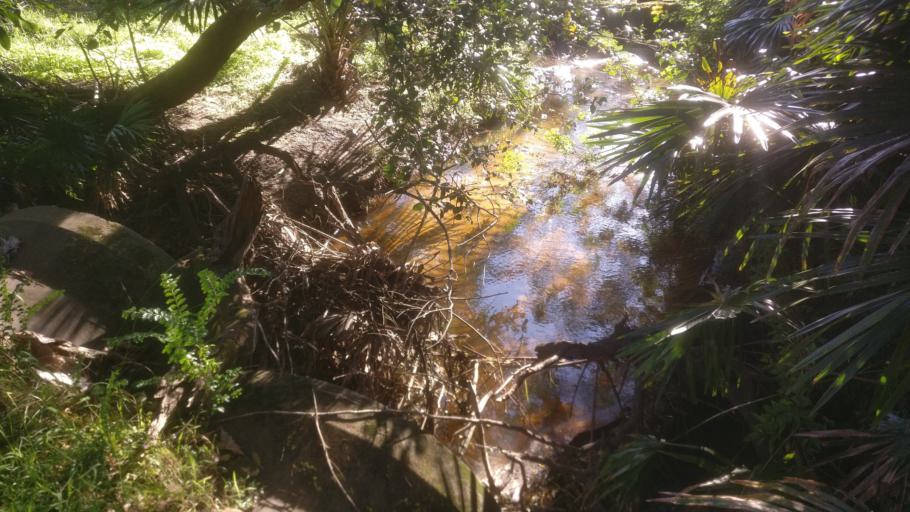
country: AU
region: New South Wales
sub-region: Pittwater
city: Ingleside
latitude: -33.7152
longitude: 151.2572
